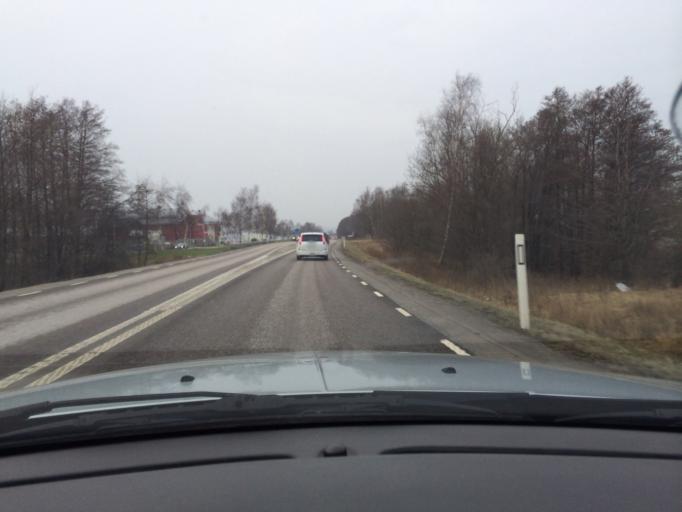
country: SE
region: Vaestra Goetaland
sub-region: Stenungsunds Kommun
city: Stenungsund
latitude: 58.0707
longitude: 11.8519
